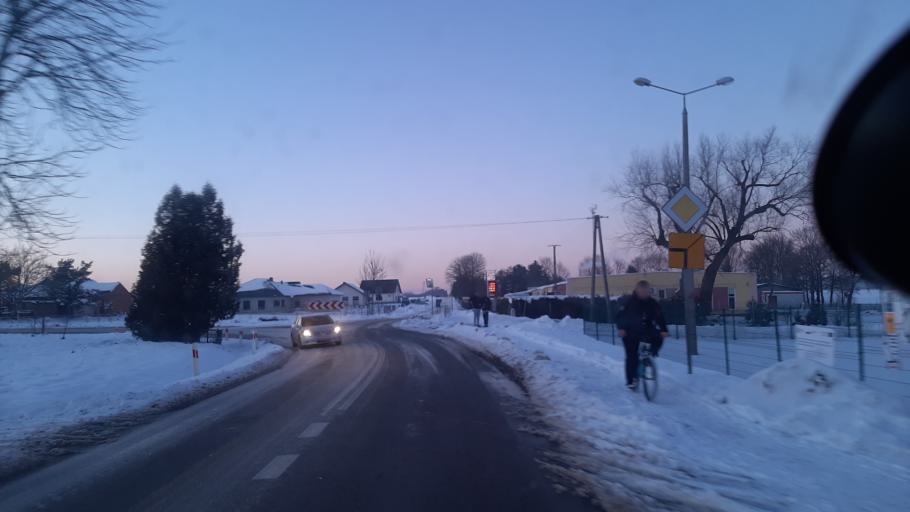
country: PL
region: Lublin Voivodeship
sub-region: Powiat lubelski
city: Niemce
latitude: 51.3622
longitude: 22.5299
